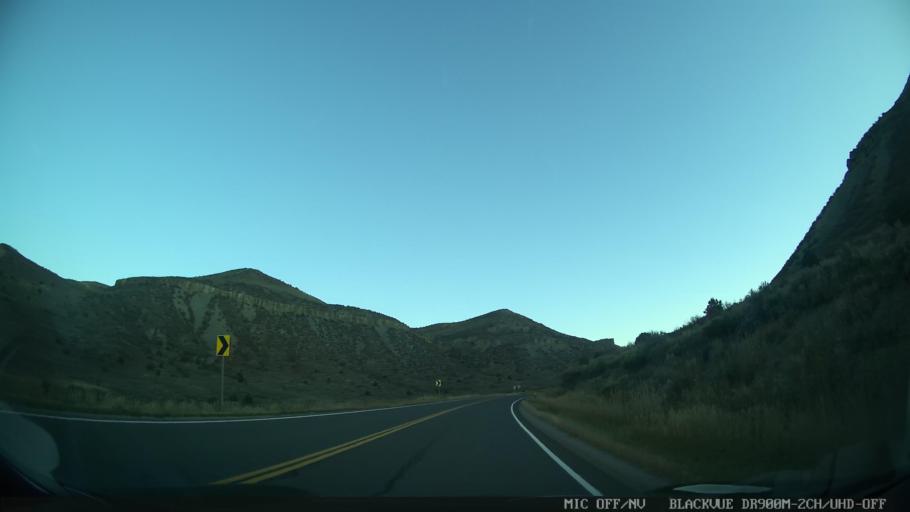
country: US
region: Colorado
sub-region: Eagle County
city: Edwards
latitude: 39.7730
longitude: -106.6833
